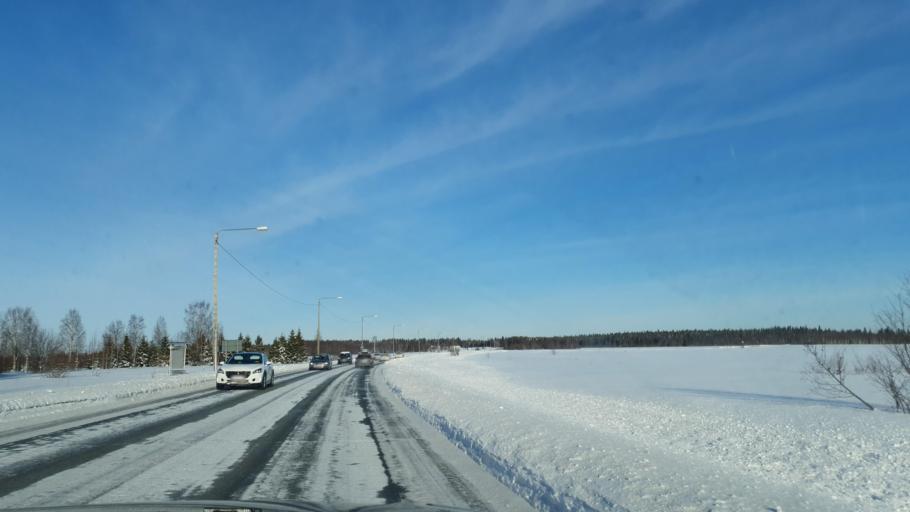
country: FI
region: Lapland
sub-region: Kemi-Tornio
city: Tornio
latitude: 65.9860
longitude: 24.0686
